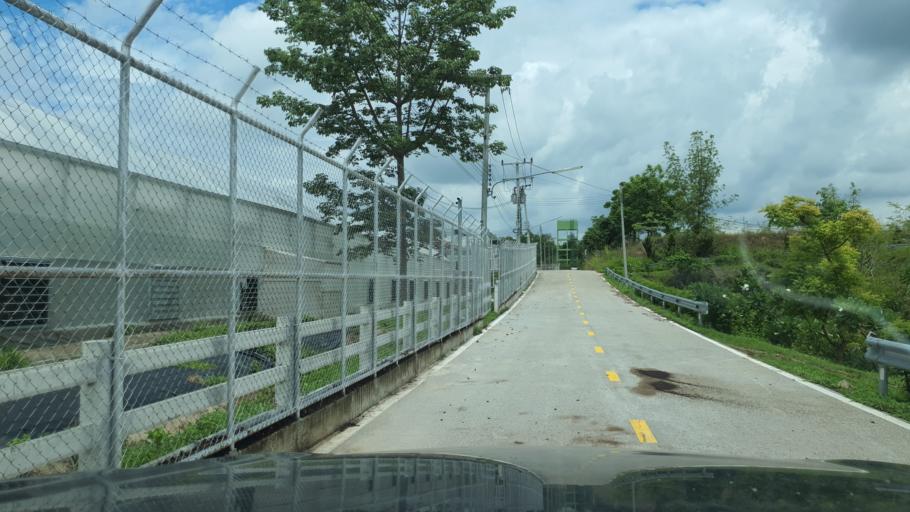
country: TH
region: Chiang Mai
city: San Sai
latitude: 18.9261
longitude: 99.0556
